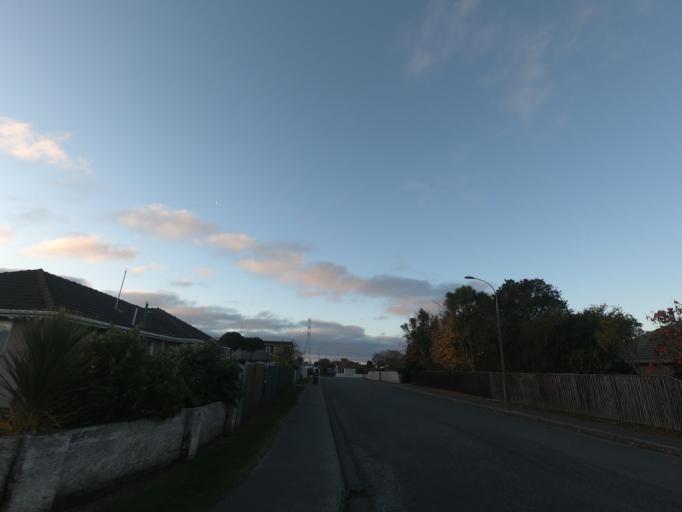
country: NZ
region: Canterbury
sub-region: Selwyn District
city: Prebbleton
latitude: -43.5745
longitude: 172.5628
